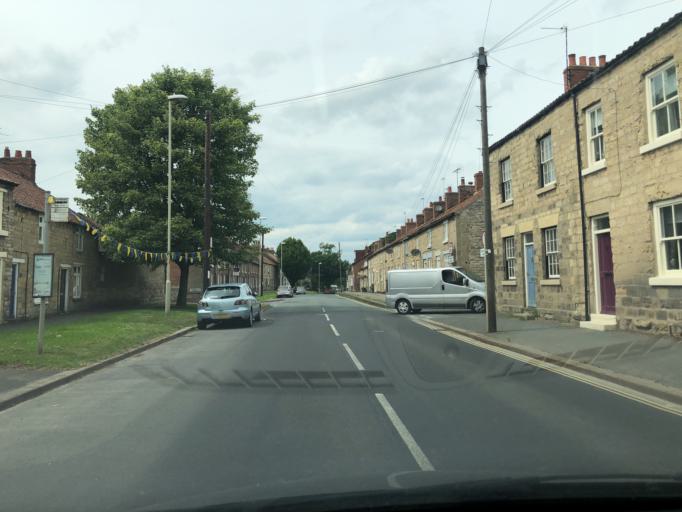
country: GB
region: England
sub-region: North Yorkshire
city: Pickering
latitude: 54.2468
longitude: -0.7876
